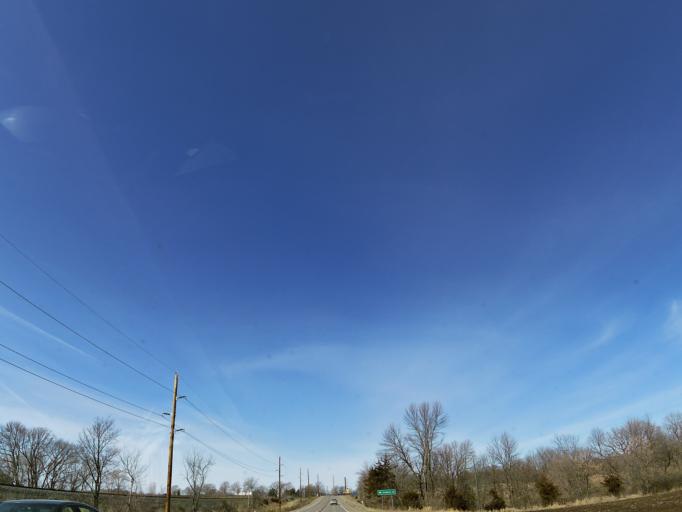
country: US
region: Minnesota
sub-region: Wright County
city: Annandale
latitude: 45.2732
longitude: -94.1739
